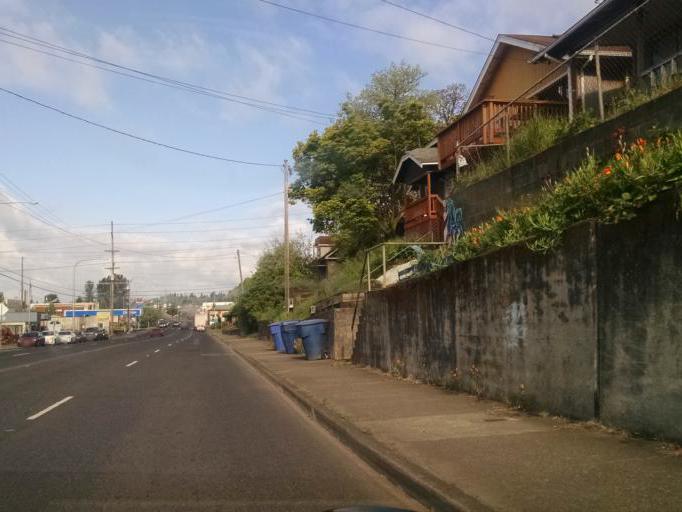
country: US
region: Washington
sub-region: Cowlitz County
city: Kelso
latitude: 46.1440
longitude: -122.9055
